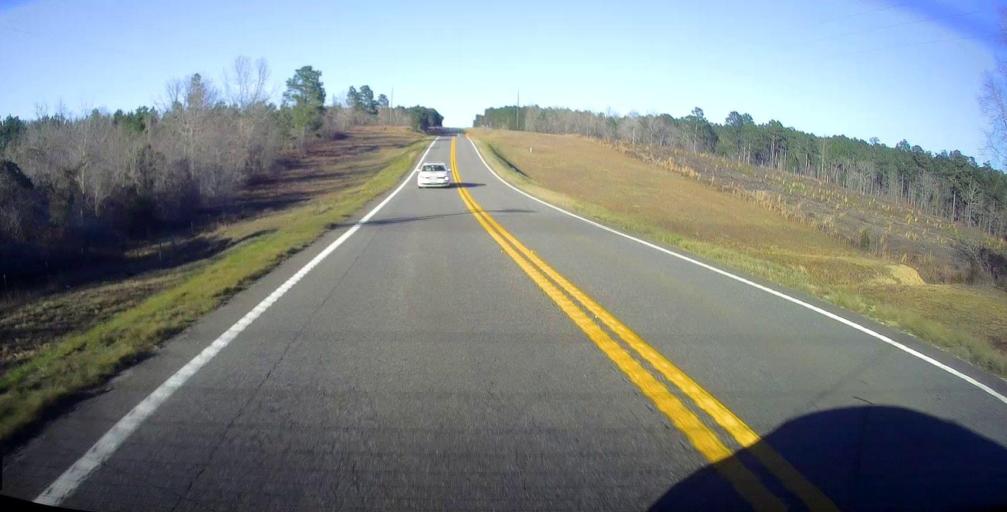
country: US
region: Georgia
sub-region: Taylor County
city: Butler
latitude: 32.4759
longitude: -84.3563
